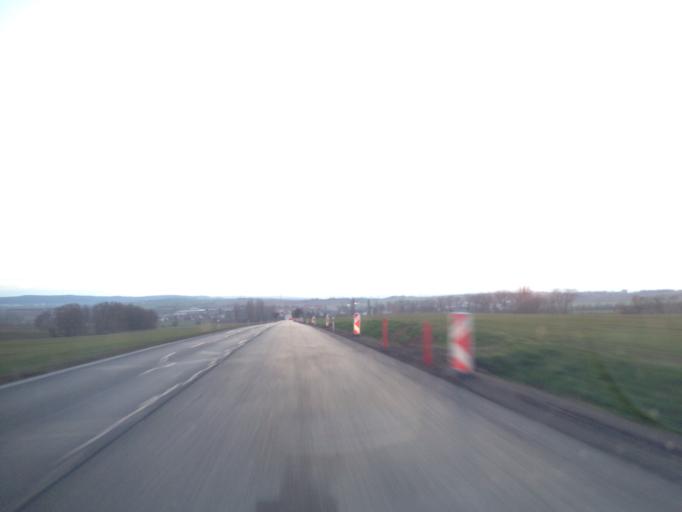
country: CZ
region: Central Bohemia
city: Rakovnik
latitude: 50.1651
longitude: 13.6226
